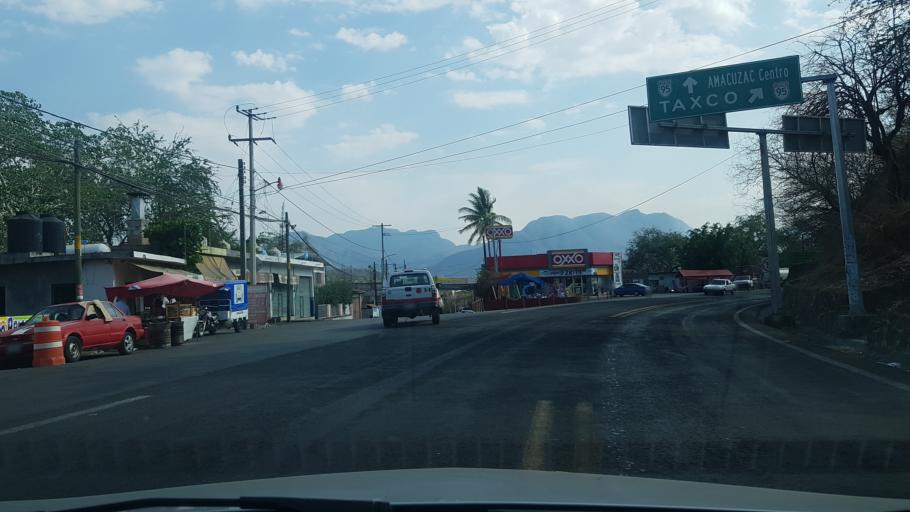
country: MX
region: Morelos
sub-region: Amacuzac
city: Amacuzac
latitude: 18.6035
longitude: -99.3687
